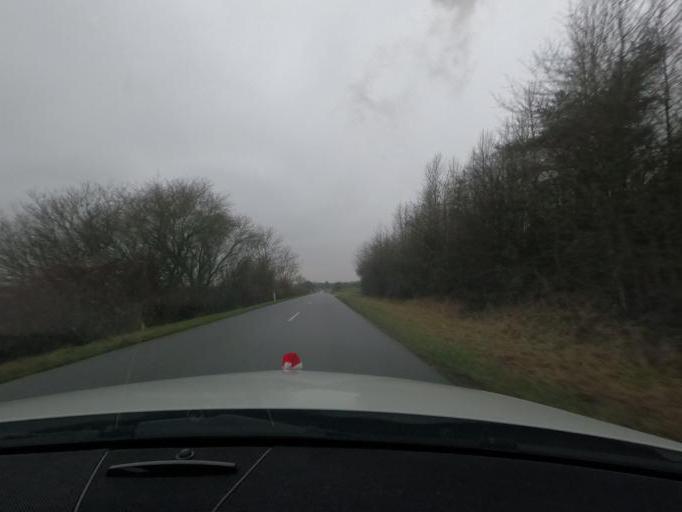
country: DK
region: South Denmark
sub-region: Haderslev Kommune
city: Haderslev
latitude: 55.1999
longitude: 9.4568
